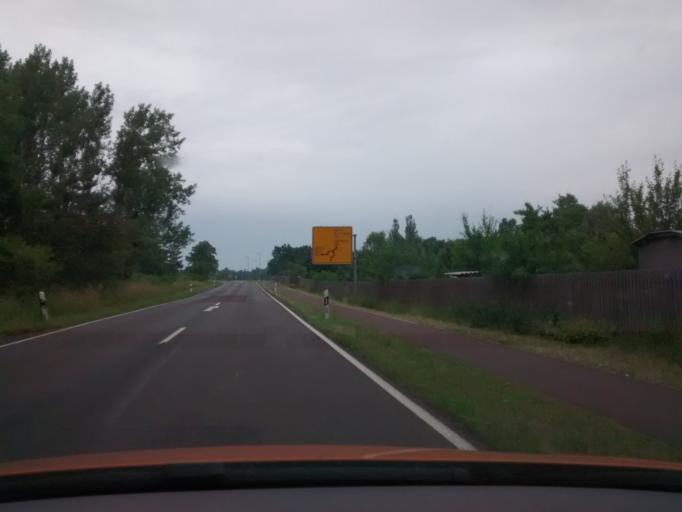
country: DE
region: Brandenburg
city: Wiesenburg
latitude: 52.1088
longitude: 12.4396
